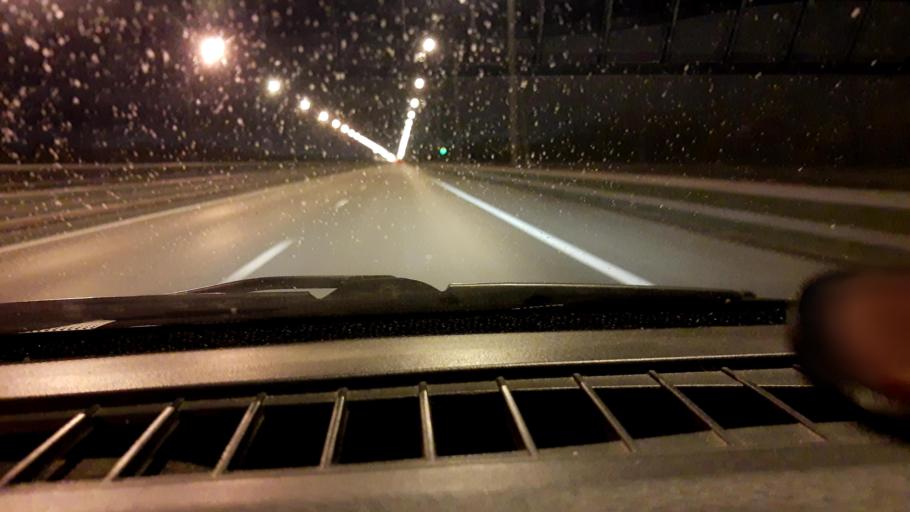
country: RU
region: Nizjnij Novgorod
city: Neklyudovo
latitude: 56.3912
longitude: 43.9791
